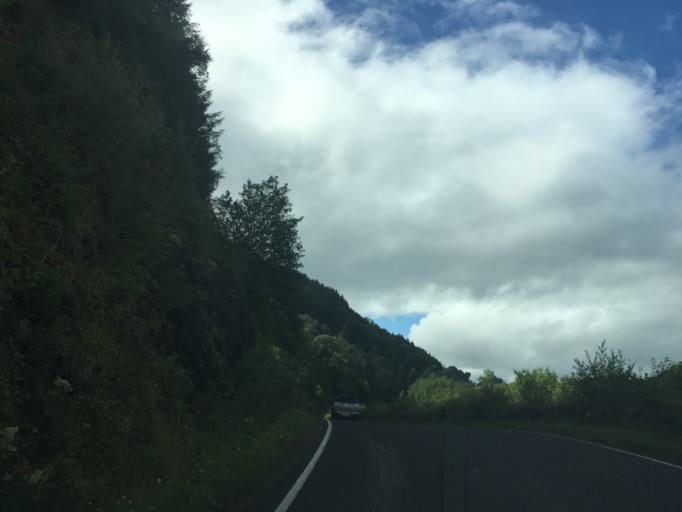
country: GB
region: Scotland
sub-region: Argyll and Bute
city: Ardrishaig
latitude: 56.0788
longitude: -5.5459
